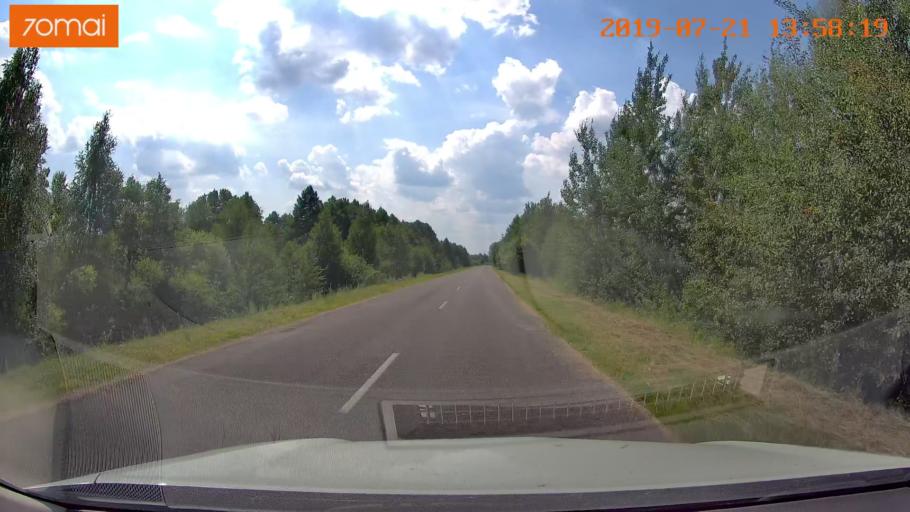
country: BY
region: Grodnenskaya
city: Lyubcha
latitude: 53.7622
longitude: 26.0821
